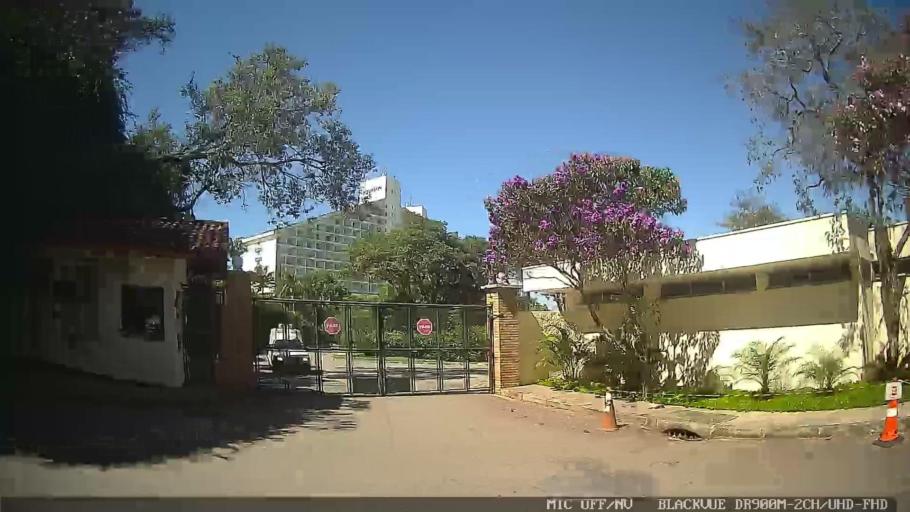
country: BR
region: Sao Paulo
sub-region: Atibaia
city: Atibaia
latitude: -23.1057
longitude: -46.5716
